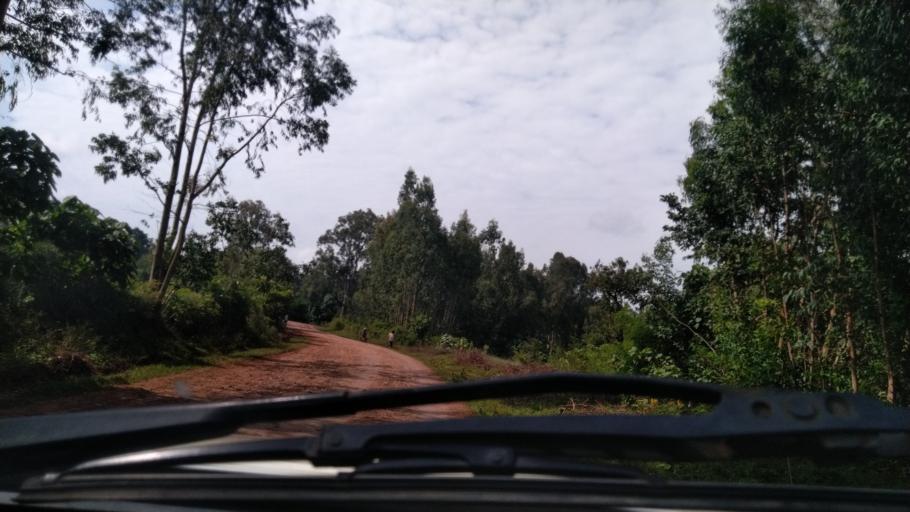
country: ET
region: Oromiya
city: Jima
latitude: 7.6519
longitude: 37.2497
